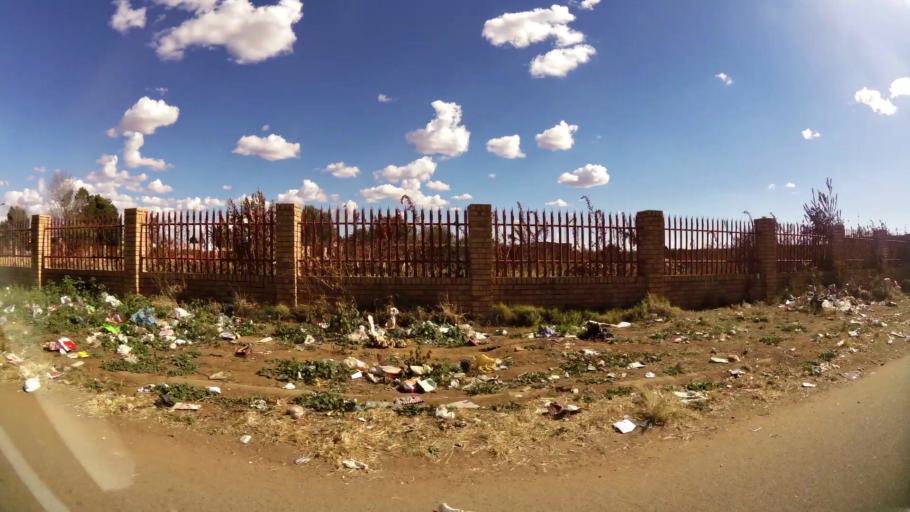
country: ZA
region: North-West
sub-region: Dr Kenneth Kaunda District Municipality
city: Klerksdorp
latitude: -26.8713
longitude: 26.5842
